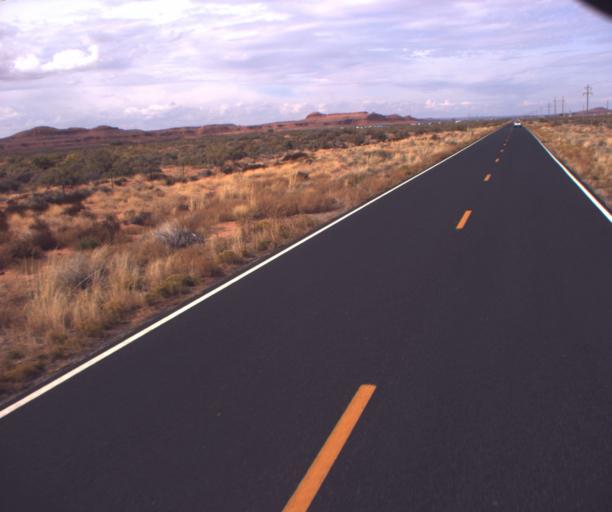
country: US
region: Arizona
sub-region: Apache County
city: Many Farms
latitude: 36.6832
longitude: -109.6046
